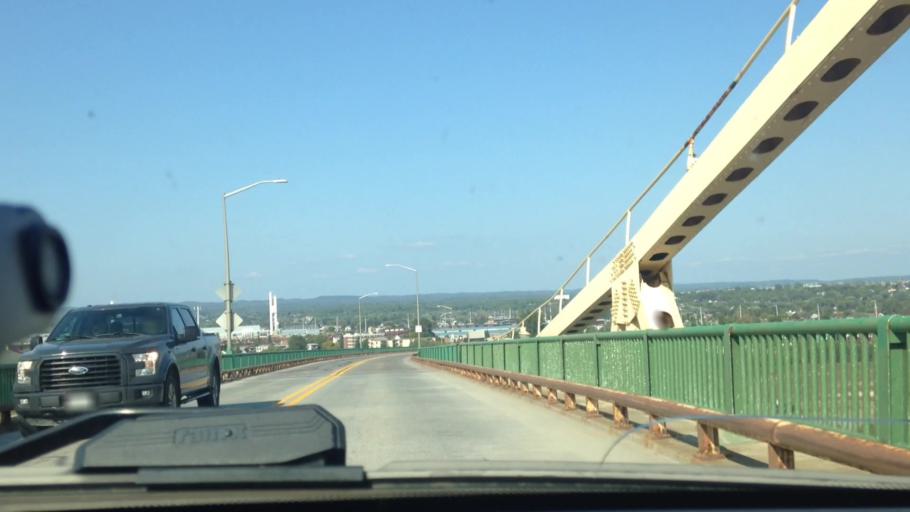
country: US
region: Michigan
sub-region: Chippewa County
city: Sault Ste. Marie
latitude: 46.5136
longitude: -84.3586
